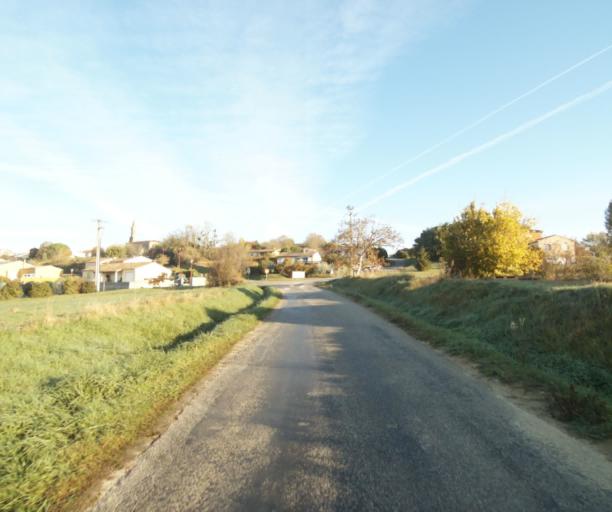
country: FR
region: Midi-Pyrenees
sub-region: Departement de la Haute-Garonne
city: Villemur-sur-Tarn
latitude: 43.8986
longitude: 1.4977
